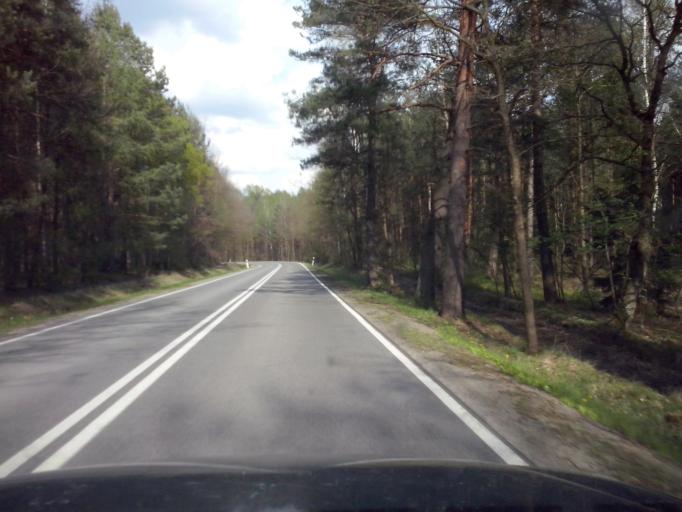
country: PL
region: Subcarpathian Voivodeship
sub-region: Powiat nizanski
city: Rudnik nad Sanem
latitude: 50.3890
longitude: 22.2680
